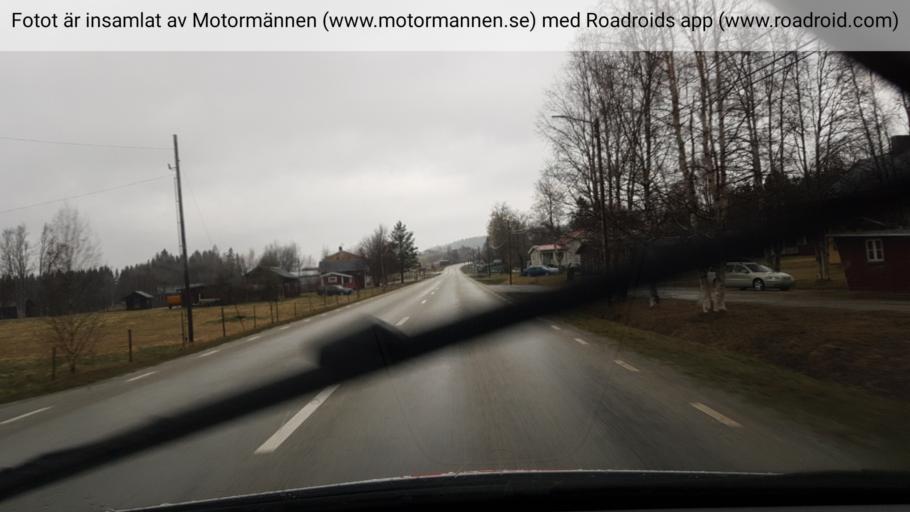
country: SE
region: Jaemtland
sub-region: Bergs Kommun
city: Hoverberg
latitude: 62.5176
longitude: 14.1940
